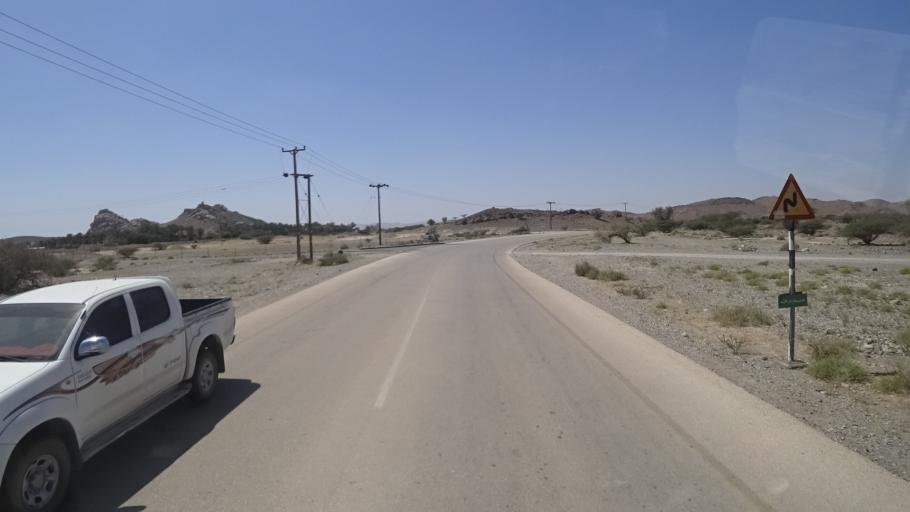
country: OM
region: Az Zahirah
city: `Ibri
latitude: 23.1466
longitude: 56.9022
